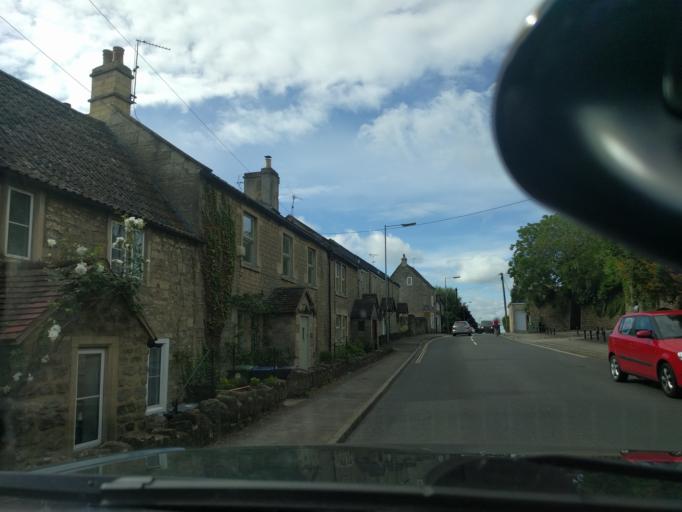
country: GB
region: England
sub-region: Wiltshire
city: Bradford-on-Avon
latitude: 51.3521
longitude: -2.2463
